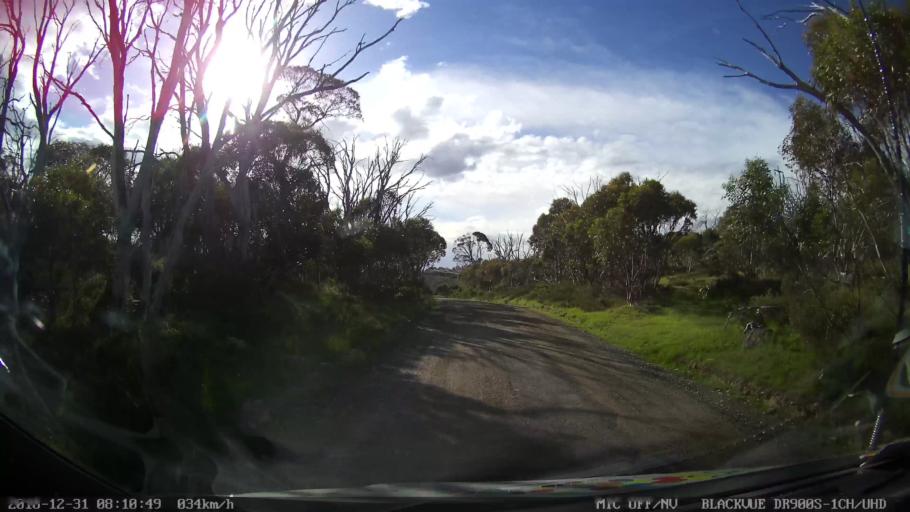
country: AU
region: New South Wales
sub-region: Snowy River
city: Jindabyne
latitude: -36.3840
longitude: 148.4232
